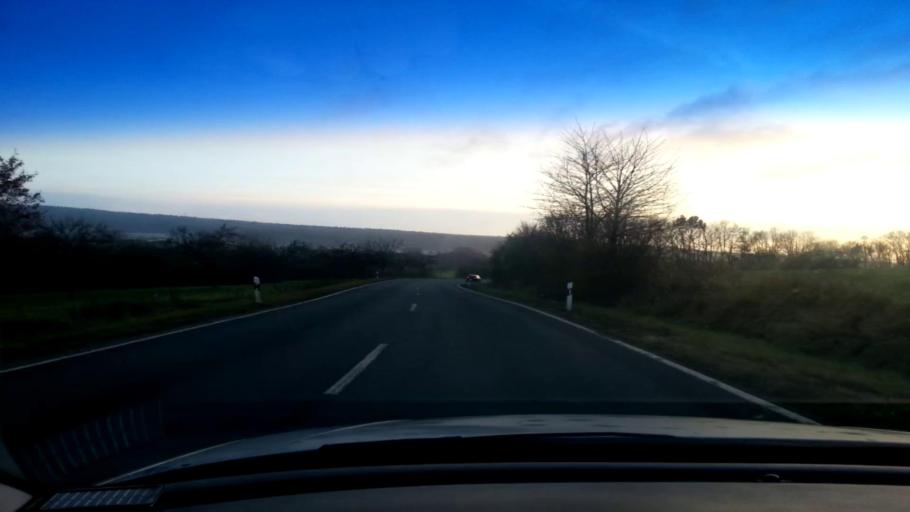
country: DE
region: Bavaria
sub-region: Upper Franconia
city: Frensdorf
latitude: 49.7923
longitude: 10.8797
